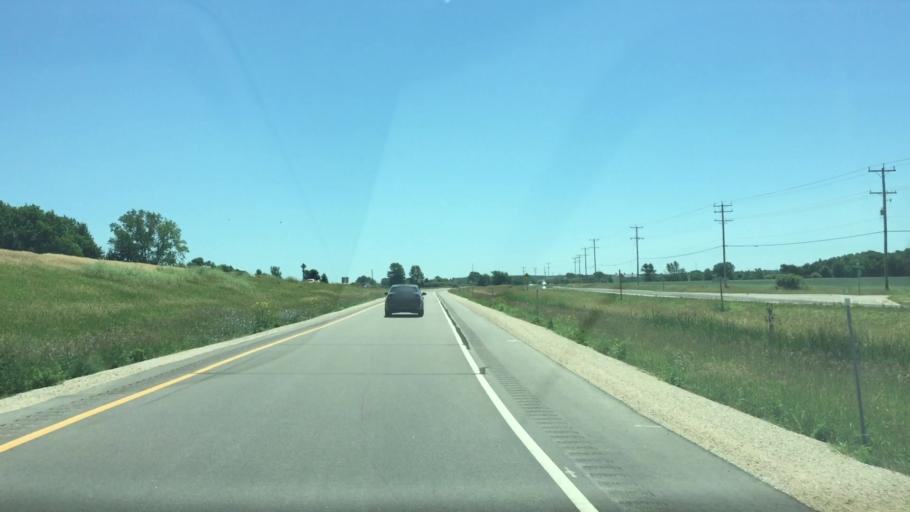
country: US
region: Wisconsin
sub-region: Outagamie County
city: Combined Locks
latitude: 44.2068
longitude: -88.3336
